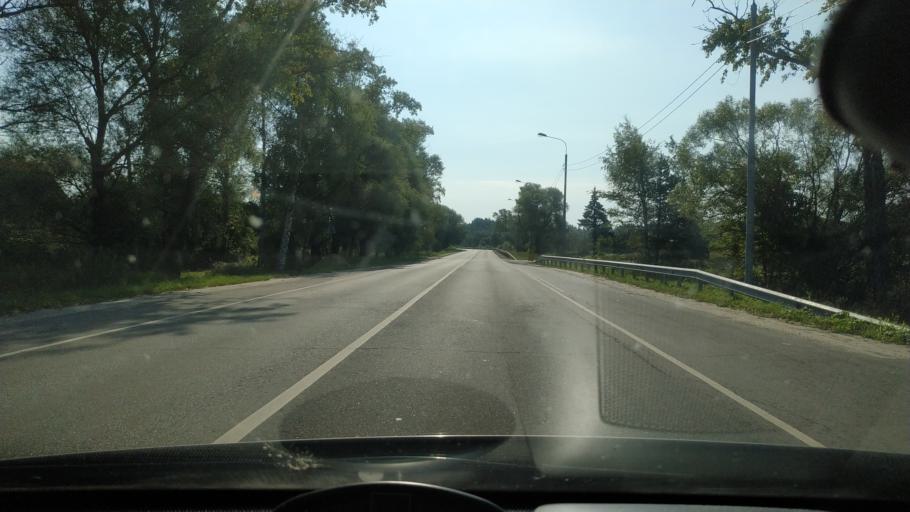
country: RU
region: Moskovskaya
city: Dmitrovskiy Pogost
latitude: 55.2335
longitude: 39.9090
